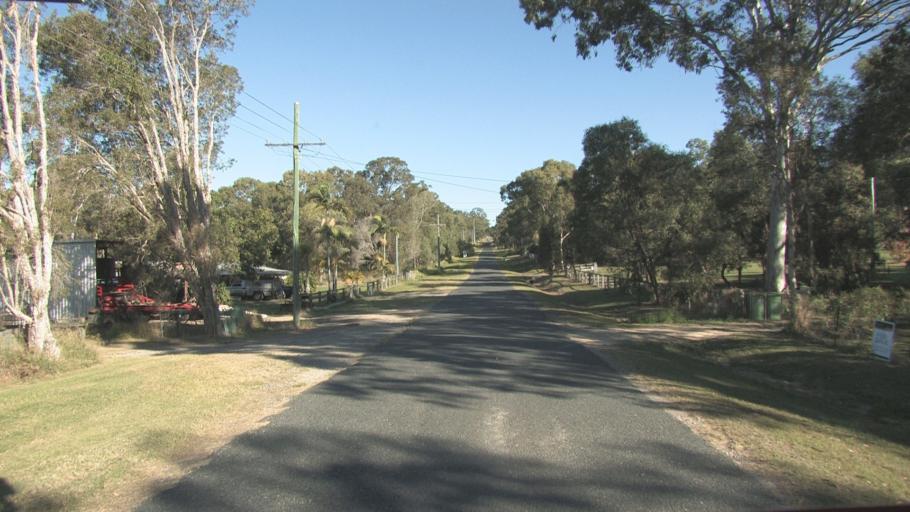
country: AU
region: Queensland
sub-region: Logan
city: Logan Reserve
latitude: -27.7206
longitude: 153.1063
